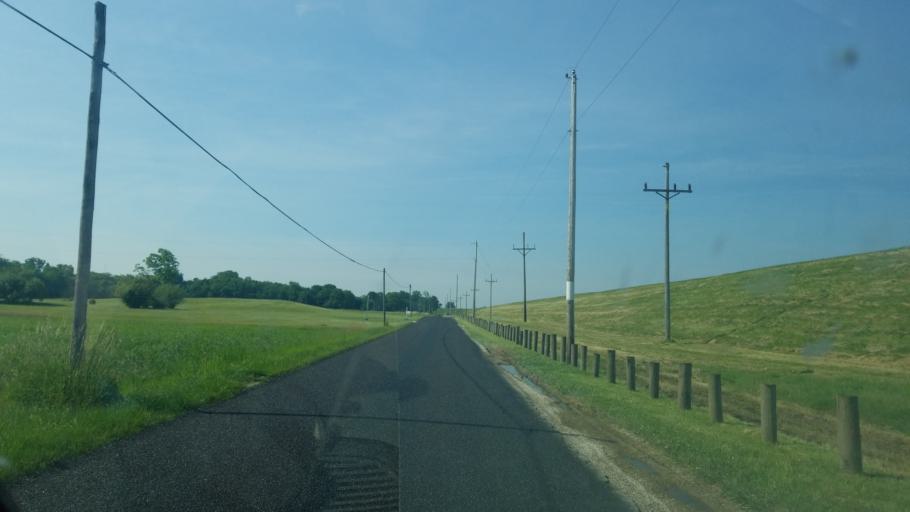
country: US
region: Ohio
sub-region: Hancock County
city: Findlay
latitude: 41.0266
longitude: -83.5595
